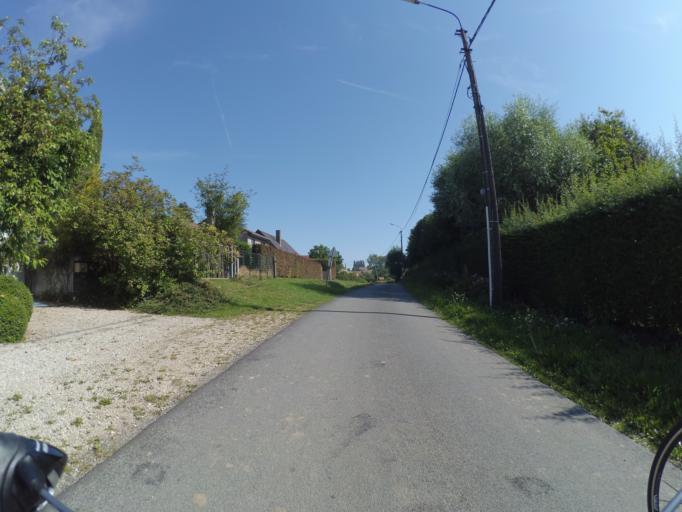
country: BE
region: Flanders
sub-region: Provincie Oost-Vlaanderen
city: Ronse
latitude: 50.7618
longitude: 3.6119
